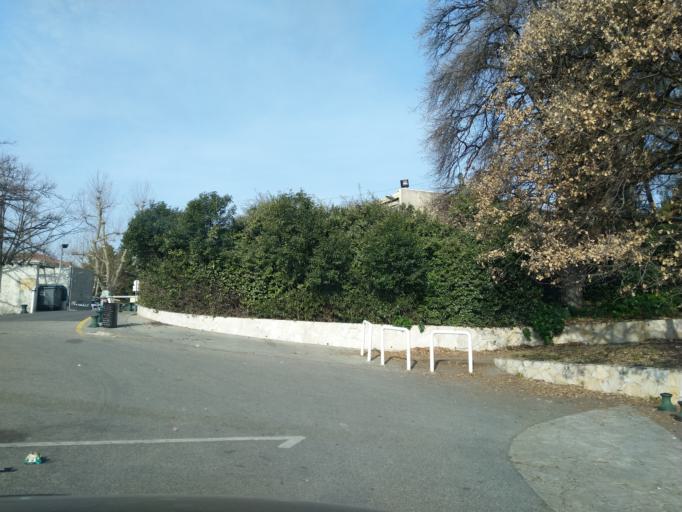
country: FR
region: Provence-Alpes-Cote d'Azur
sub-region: Departement des Bouches-du-Rhone
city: Marseille 12
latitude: 43.2973
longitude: 5.4437
